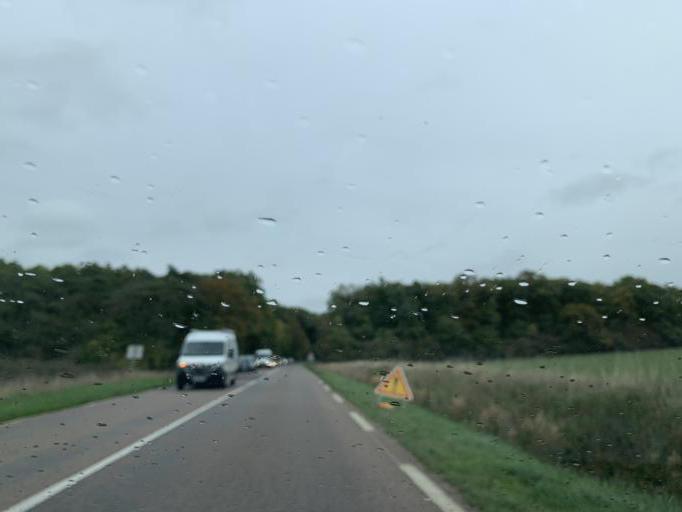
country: FR
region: Bourgogne
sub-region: Departement de l'Yonne
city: Moneteau
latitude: 47.8340
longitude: 3.5931
